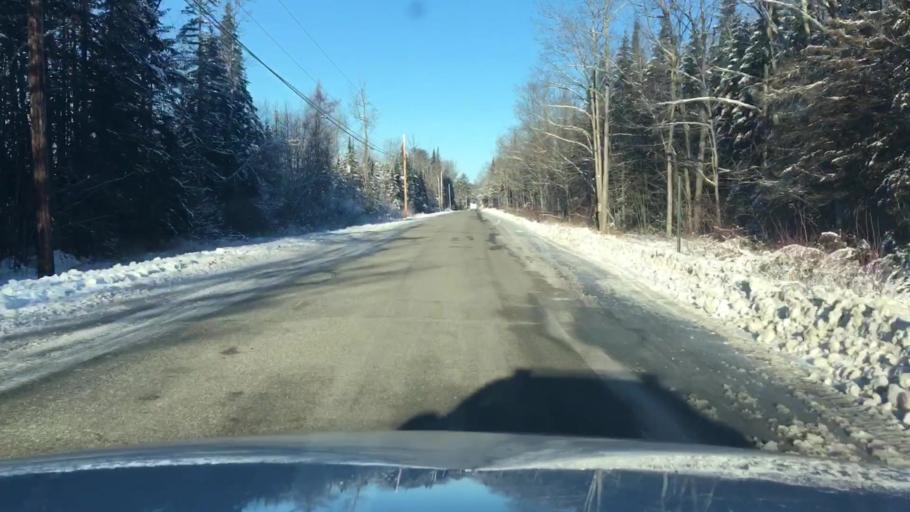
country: US
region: Maine
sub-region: Kennebec County
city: Belgrade
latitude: 44.4081
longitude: -69.8630
